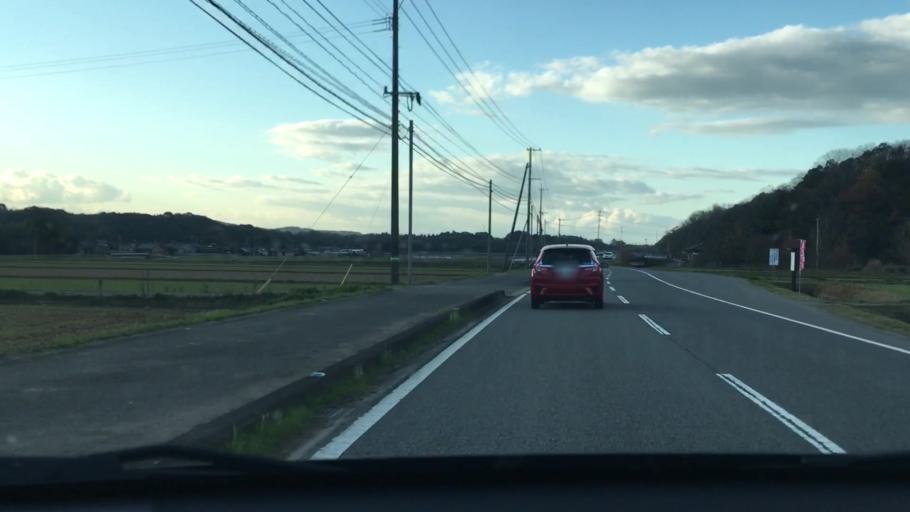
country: JP
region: Oita
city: Bungo-Takada-shi
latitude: 33.5051
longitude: 131.3638
